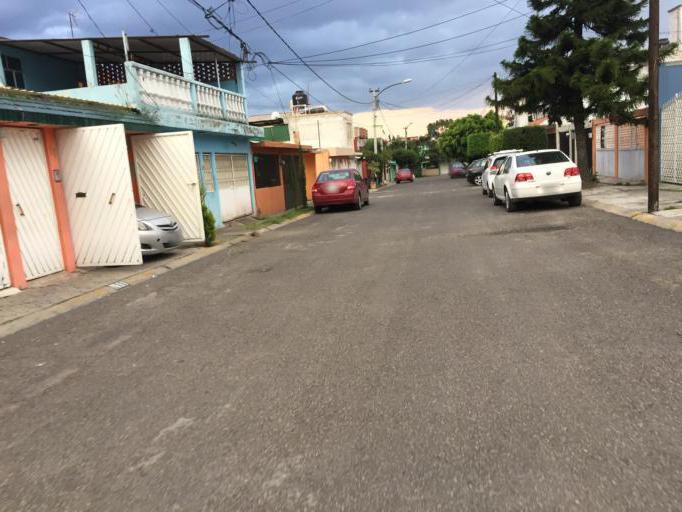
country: MX
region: Mexico
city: Cuautitlan Izcalli
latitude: 19.6502
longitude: -99.2118
